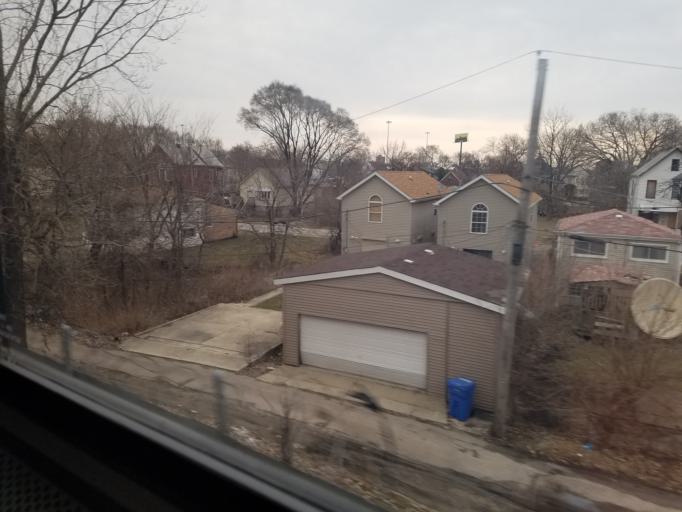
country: US
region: Illinois
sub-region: Cook County
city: Chicago
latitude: 41.7961
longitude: -87.6354
